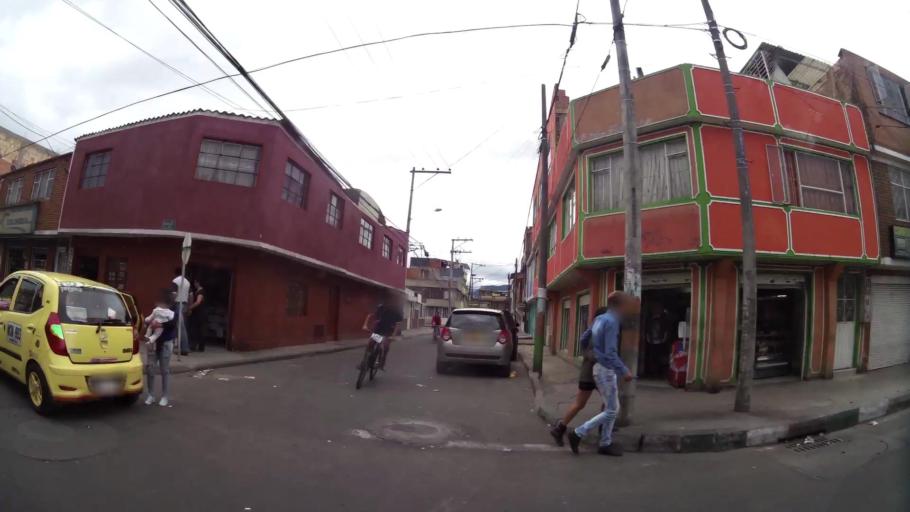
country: CO
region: Bogota D.C.
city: Bogota
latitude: 4.6023
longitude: -74.1372
